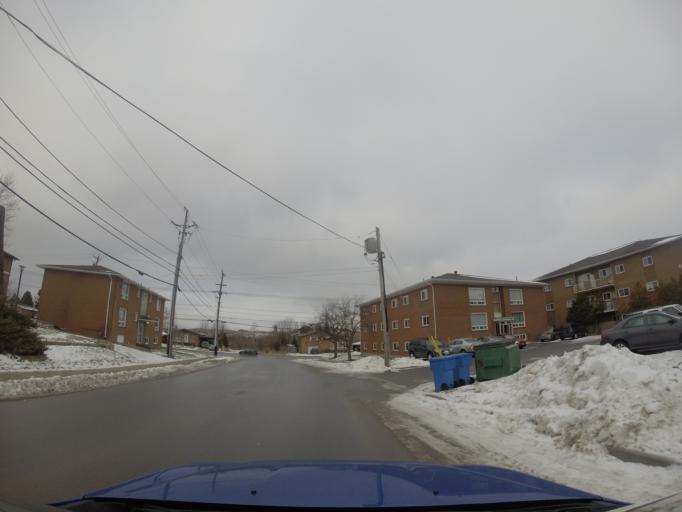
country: CA
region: Ontario
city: Greater Sudbury
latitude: 46.4622
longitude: -81.0272
